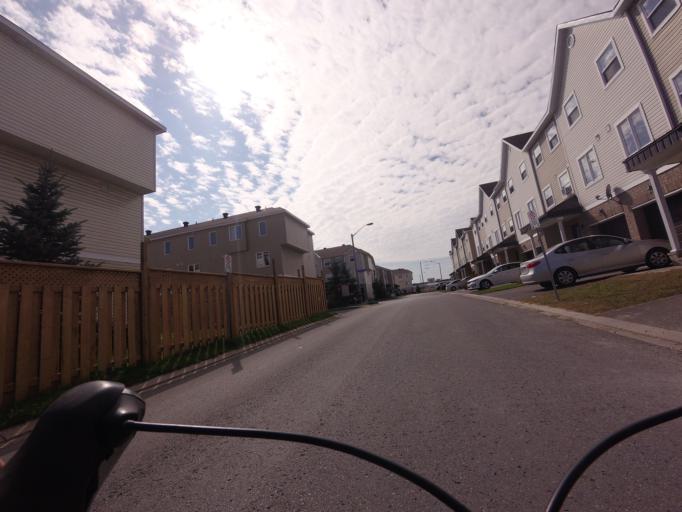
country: CA
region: Ontario
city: Bells Corners
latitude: 45.2646
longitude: -75.7759
